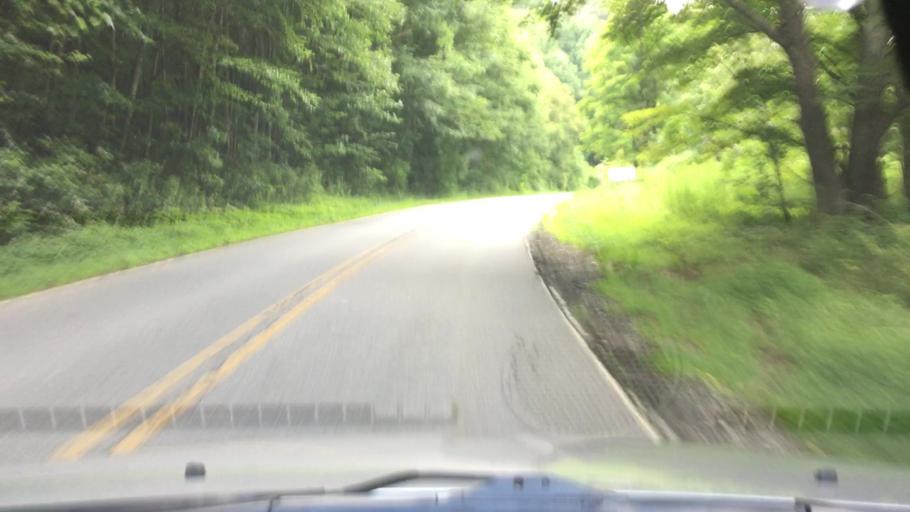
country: US
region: North Carolina
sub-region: Madison County
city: Mars Hill
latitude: 35.9248
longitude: -82.5319
